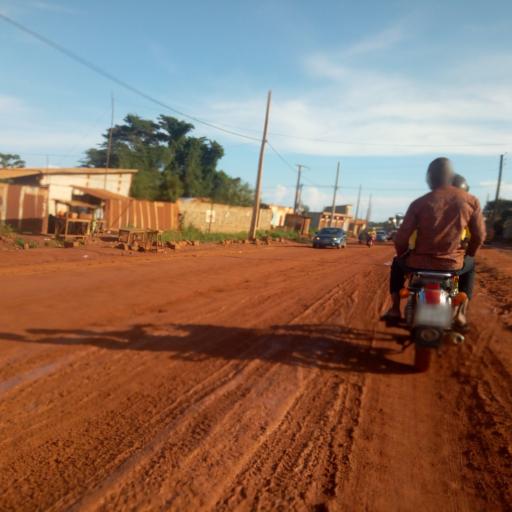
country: BJ
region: Atlantique
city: Hevie
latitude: 6.4090
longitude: 2.2655
